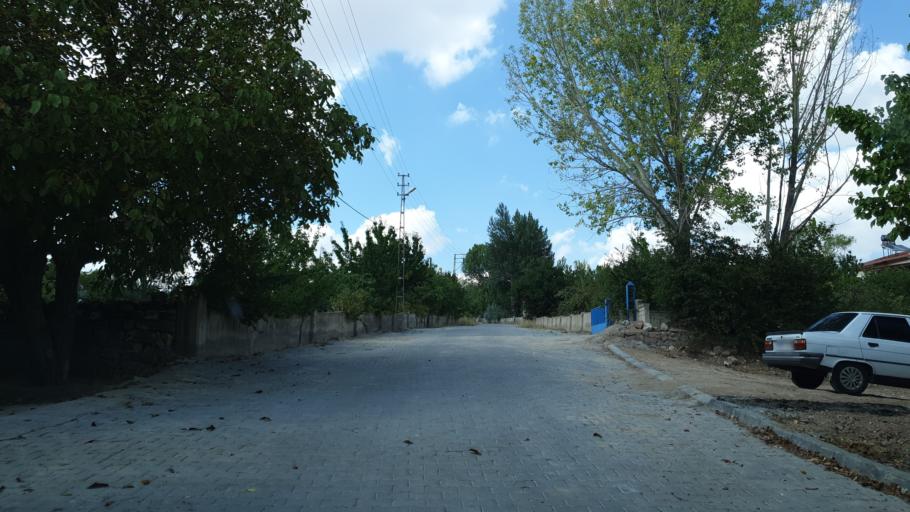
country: TR
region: Kayseri
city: Felahiye
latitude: 39.1137
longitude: 35.6104
